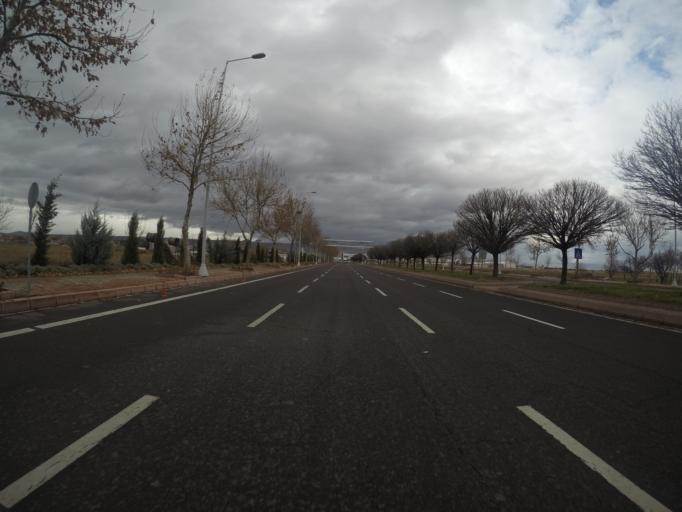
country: TR
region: Kayseri
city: Kayseri
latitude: 38.7607
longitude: 35.4821
